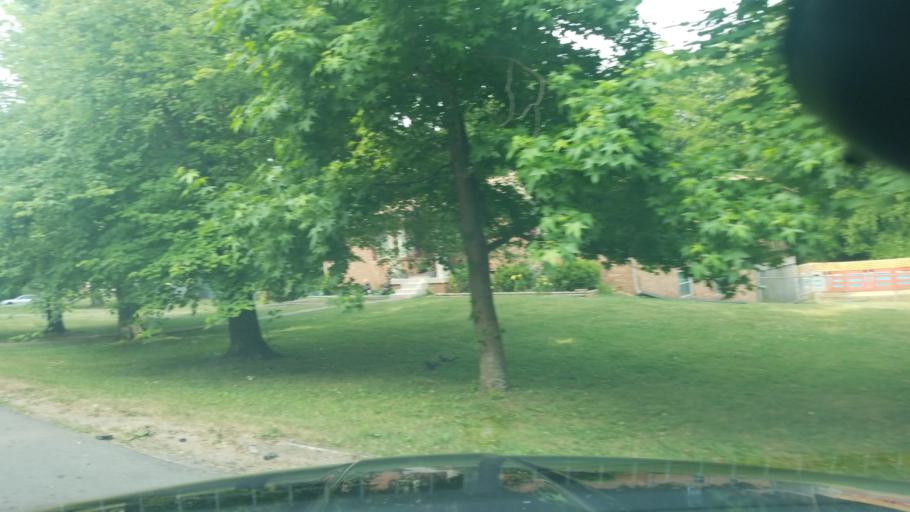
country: US
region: Tennessee
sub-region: Davidson County
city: Goodlettsville
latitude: 36.2676
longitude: -86.7546
